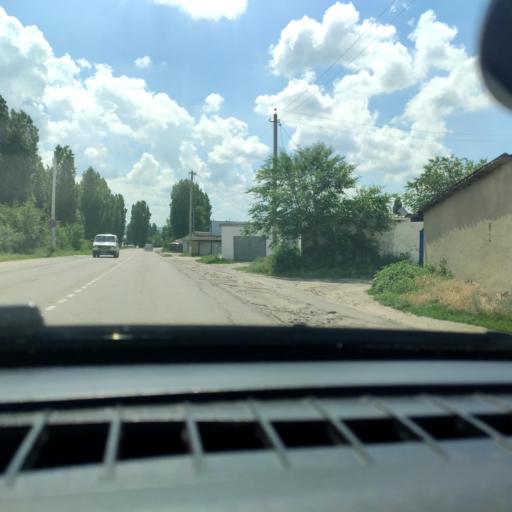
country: RU
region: Voronezj
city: Strelitsa
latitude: 51.5767
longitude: 38.7908
